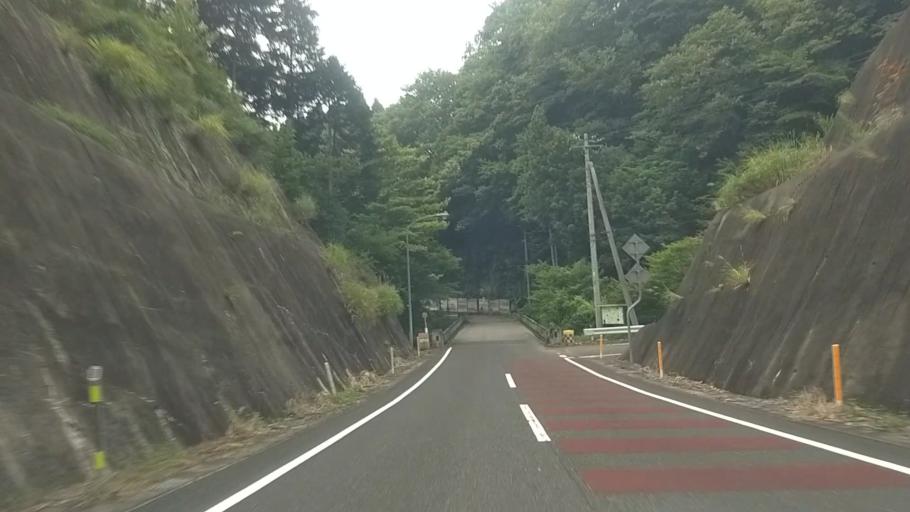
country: JP
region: Chiba
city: Kawaguchi
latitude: 35.1893
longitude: 140.1408
